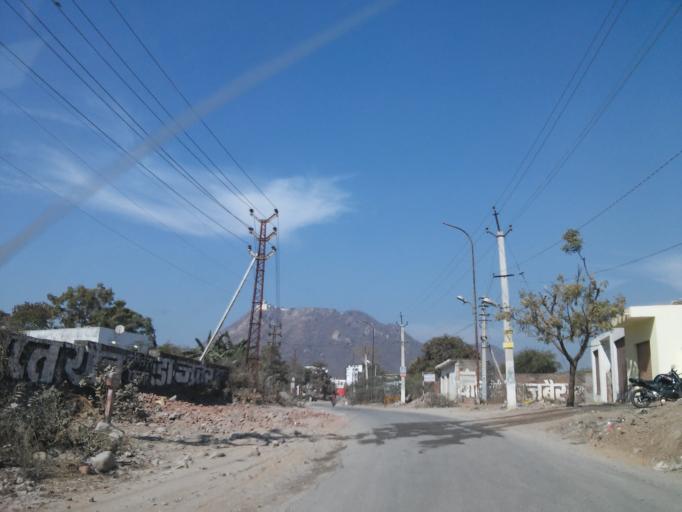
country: IN
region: Rajasthan
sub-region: Udaipur
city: Udaipur
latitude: 24.5797
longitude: 73.6540
